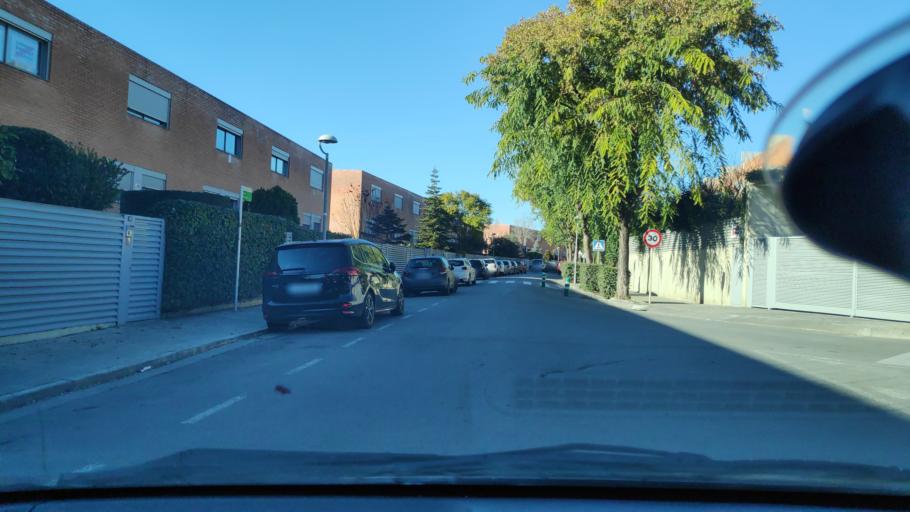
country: ES
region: Catalonia
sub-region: Provincia de Barcelona
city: Sant Quirze del Valles
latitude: 41.5406
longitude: 2.0698
